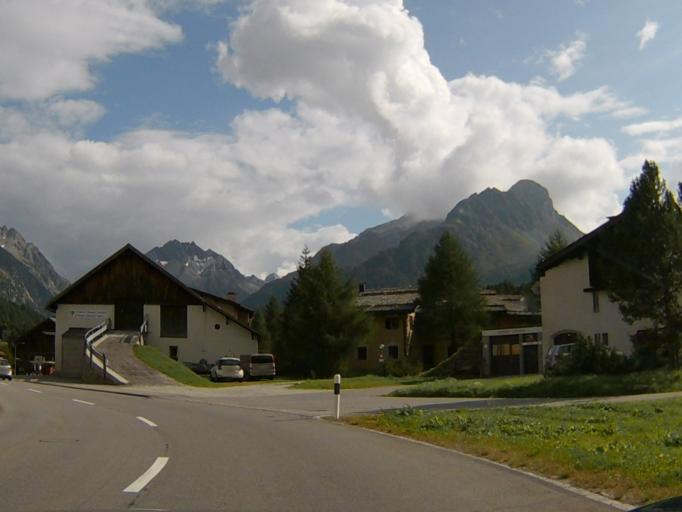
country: CH
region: Grisons
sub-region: Maloja District
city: Silvaplana
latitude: 46.4043
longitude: 9.6946
